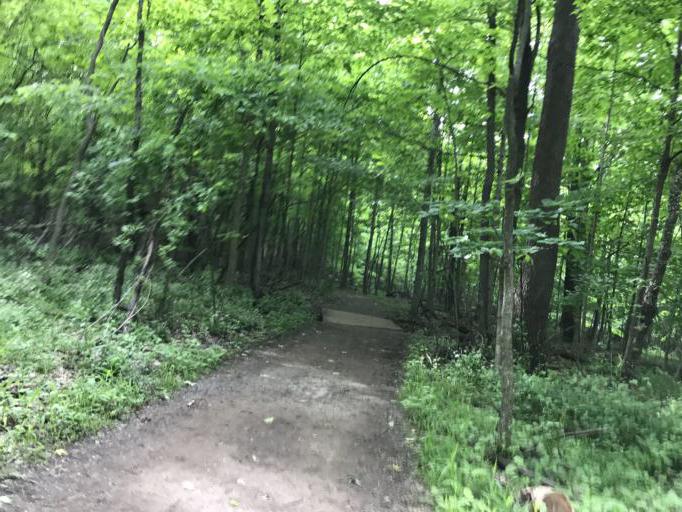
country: US
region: Michigan
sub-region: Oakland County
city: Farmington Hills
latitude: 42.4755
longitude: -83.3861
